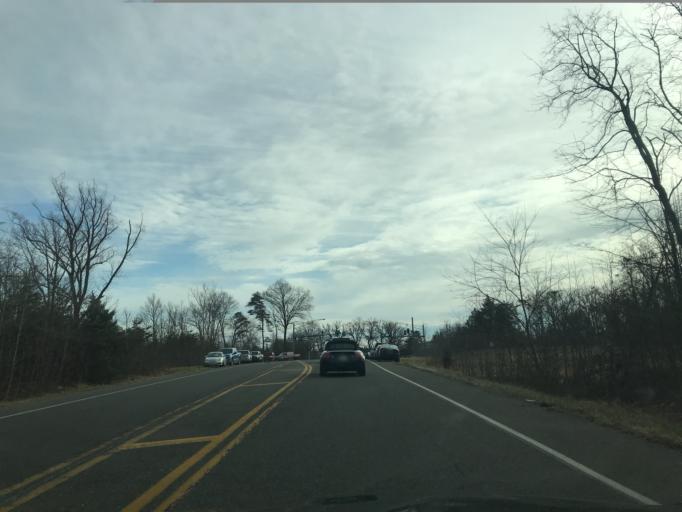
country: US
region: Maryland
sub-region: Prince George's County
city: Glenn Dale
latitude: 38.9976
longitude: -76.8341
